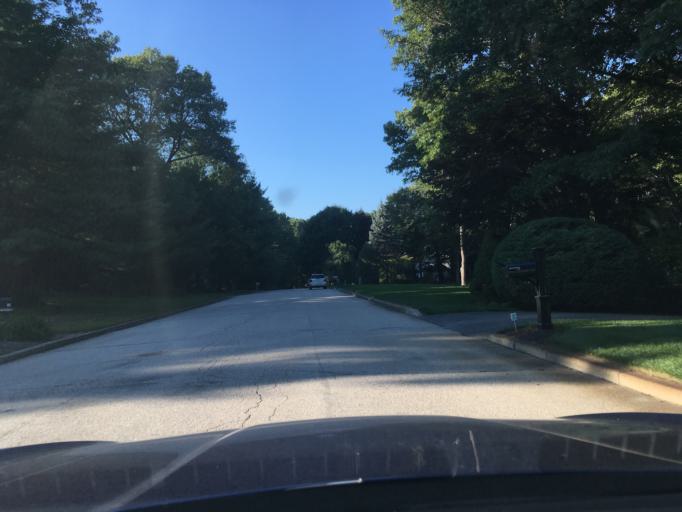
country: US
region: Rhode Island
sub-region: Kent County
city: West Warwick
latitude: 41.6473
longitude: -71.5161
